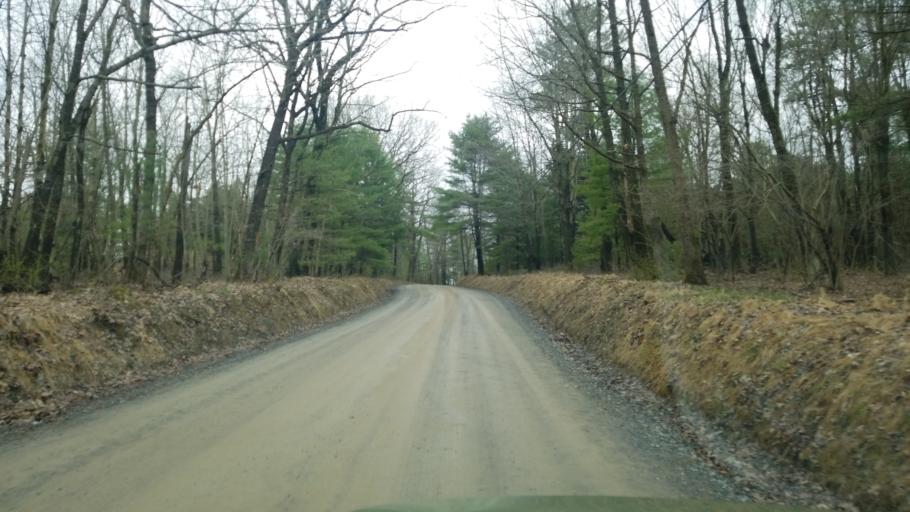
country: US
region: Pennsylvania
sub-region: Clearfield County
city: Shiloh
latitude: 41.1425
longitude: -78.3360
